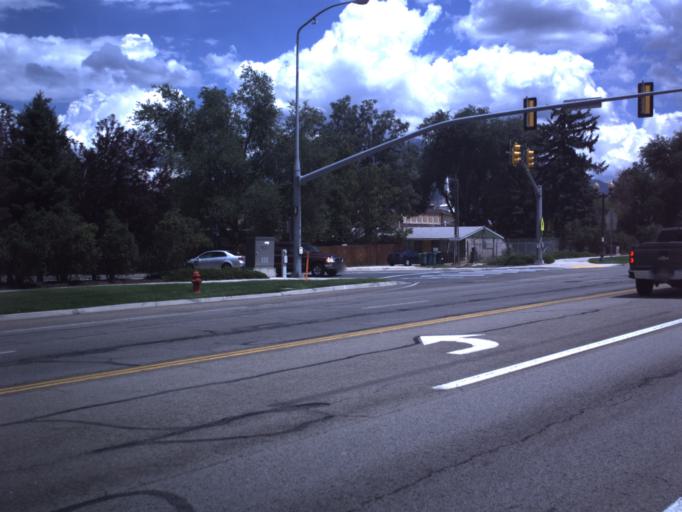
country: US
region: Utah
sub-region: Salt Lake County
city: Sandy City
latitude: 40.5881
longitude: -111.8825
